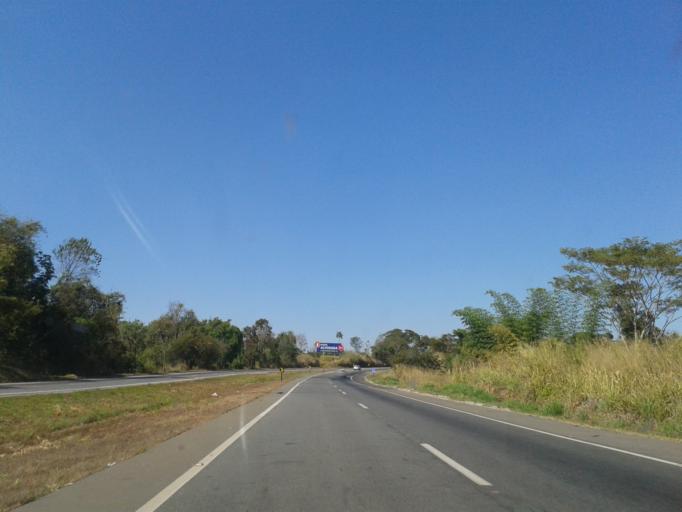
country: BR
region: Goias
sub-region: Piracanjuba
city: Piracanjuba
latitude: -17.2250
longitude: -49.2294
